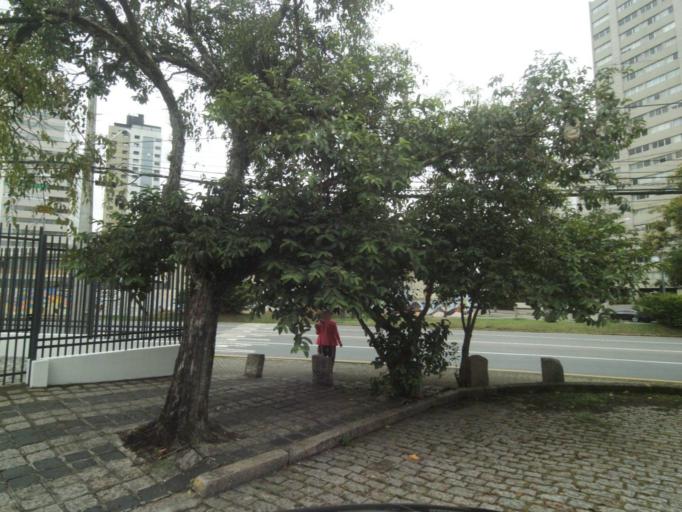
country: BR
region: Parana
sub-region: Curitiba
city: Curitiba
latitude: -25.4178
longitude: -49.2645
